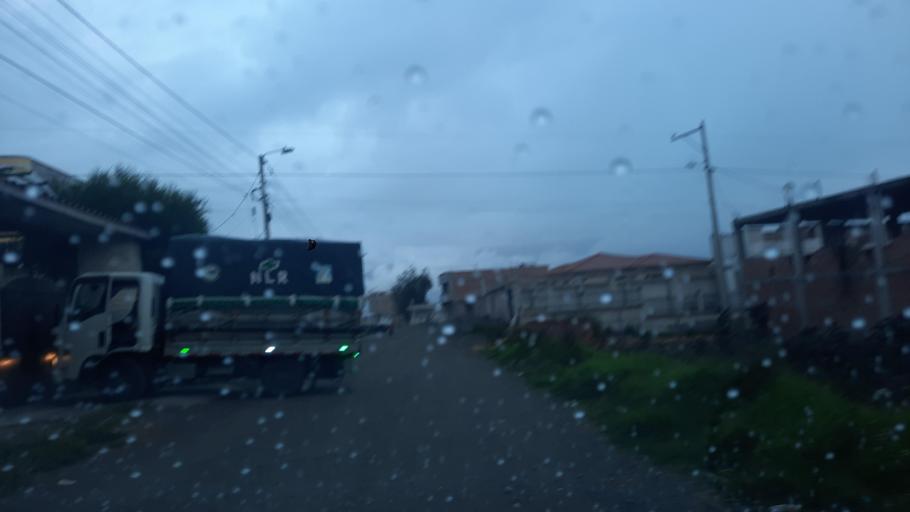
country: EC
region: Chimborazo
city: Riobamba
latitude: -1.6878
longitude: -78.6617
